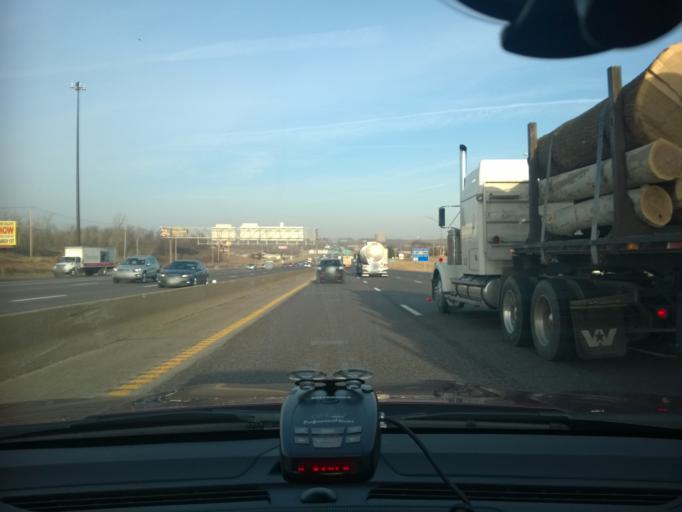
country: US
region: Missouri
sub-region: Saint Louis County
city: Bridgeton
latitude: 38.7509
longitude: -90.4458
